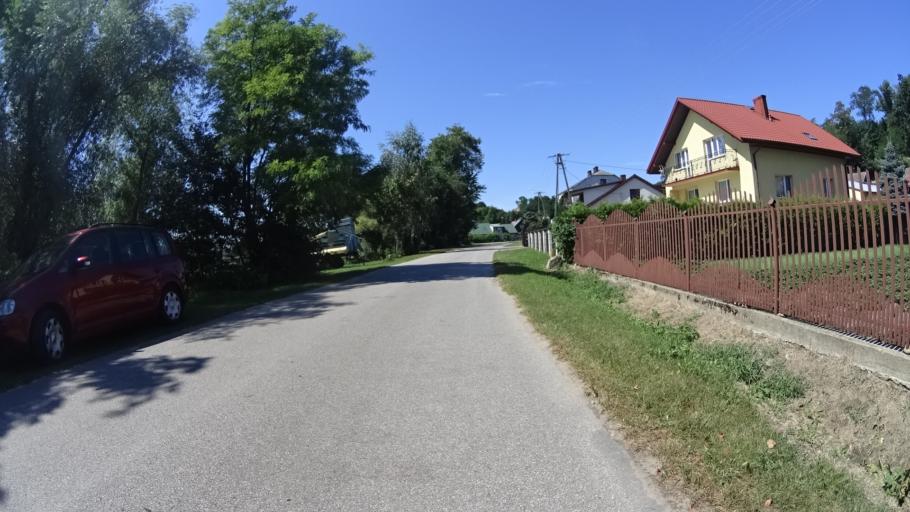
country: PL
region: Masovian Voivodeship
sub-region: Powiat bialobrzeski
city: Bialobrzegi
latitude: 51.6660
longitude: 20.8899
